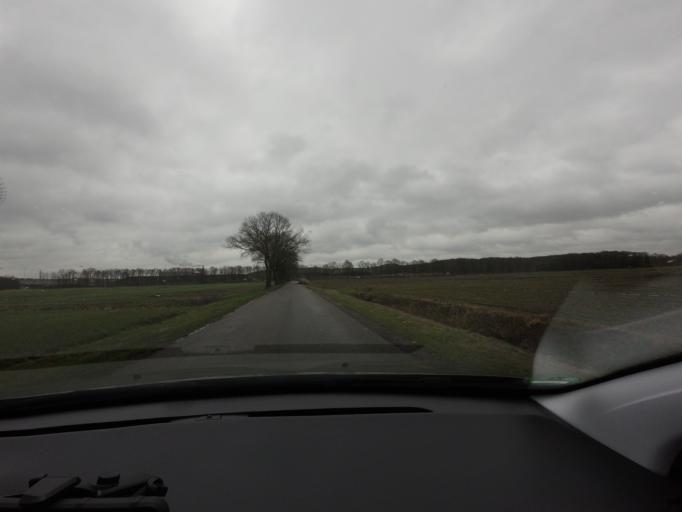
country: NL
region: Drenthe
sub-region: Gemeente Hoogeveen
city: Hoogeveen
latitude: 52.7794
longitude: 6.5060
